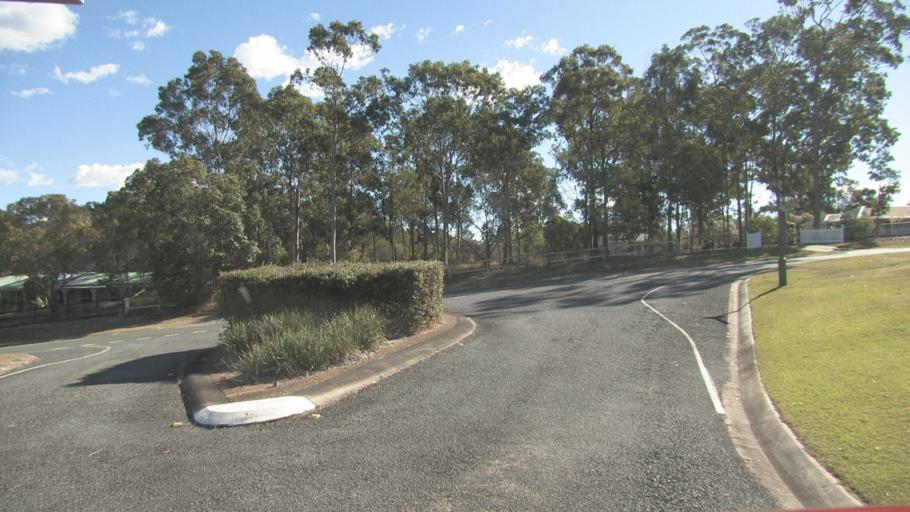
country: AU
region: Queensland
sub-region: Ipswich
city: Springfield Lakes
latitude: -27.7370
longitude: 152.9195
